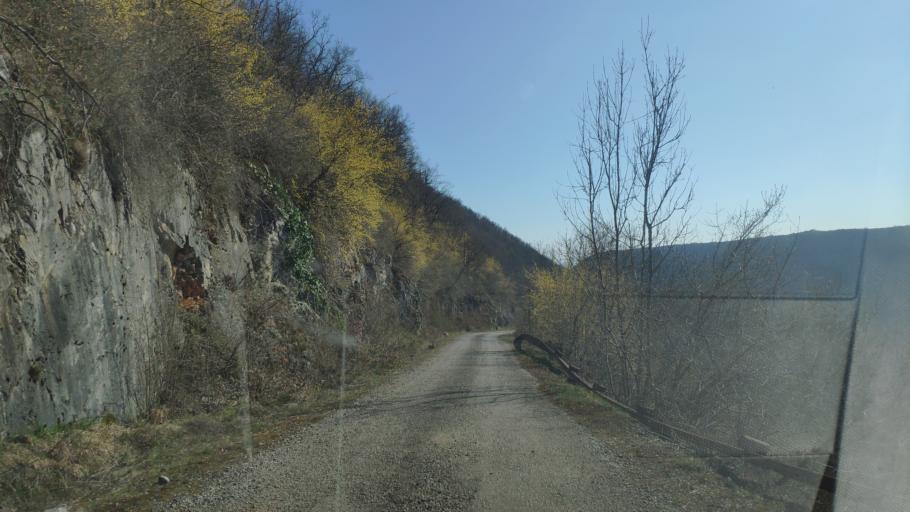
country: SK
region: Kosicky
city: Roznava
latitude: 48.5732
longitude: 20.4060
